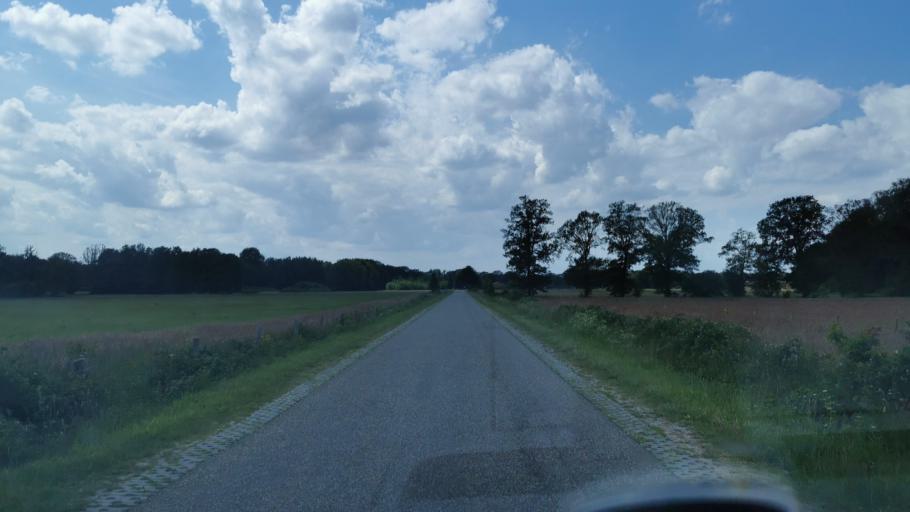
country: NL
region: Overijssel
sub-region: Gemeente Hengelo
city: Hengelo
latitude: 52.3234
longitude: 6.8484
